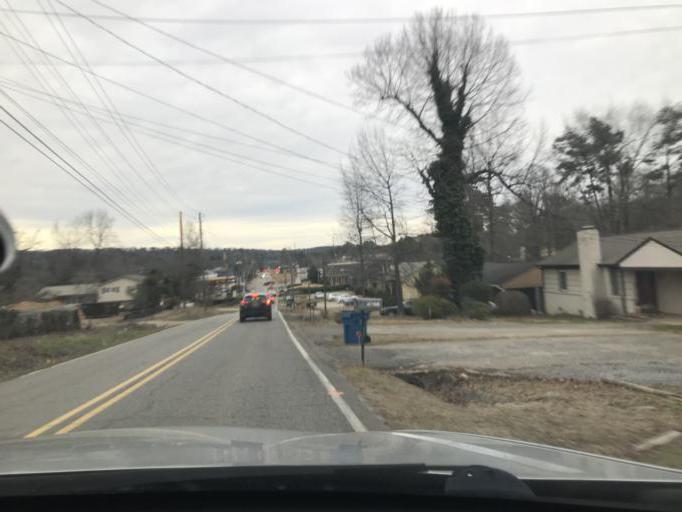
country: US
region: Alabama
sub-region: Jefferson County
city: Cahaba Heights
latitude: 33.4578
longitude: -86.7310
